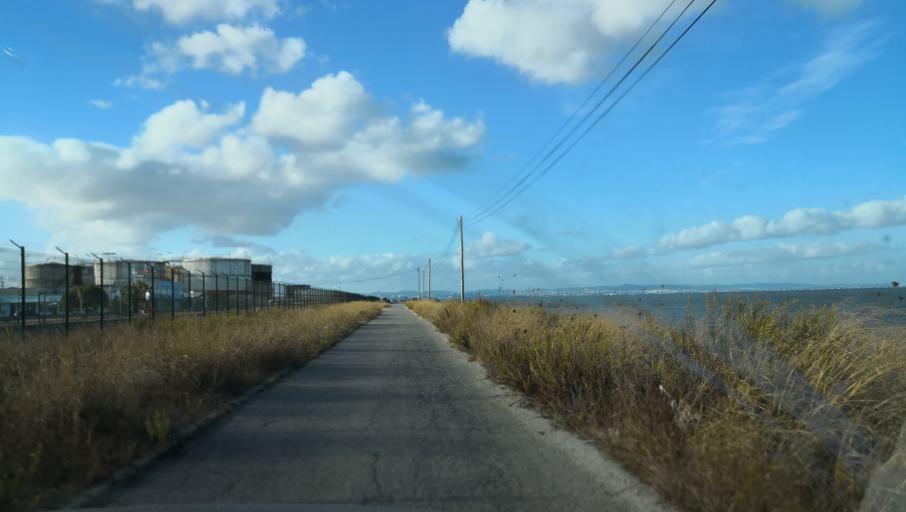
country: PT
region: Setubal
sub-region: Barreiro
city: Barreiro
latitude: 38.6806
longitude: -9.0563
